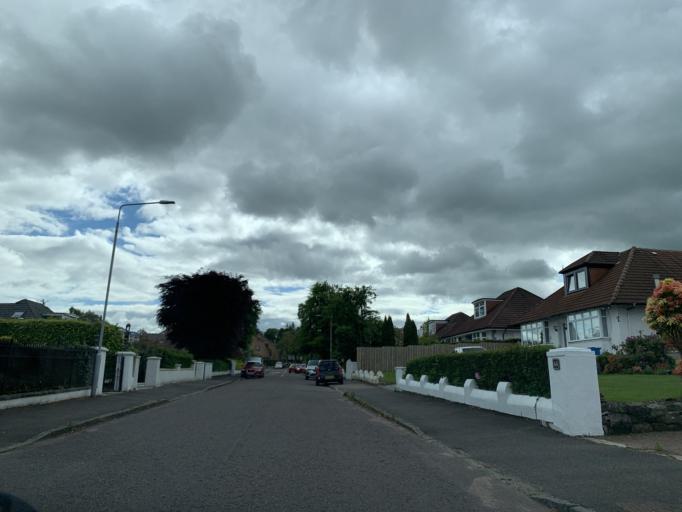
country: GB
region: Scotland
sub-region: East Renfrewshire
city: Newton Mearns
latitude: 55.7742
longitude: -4.3270
